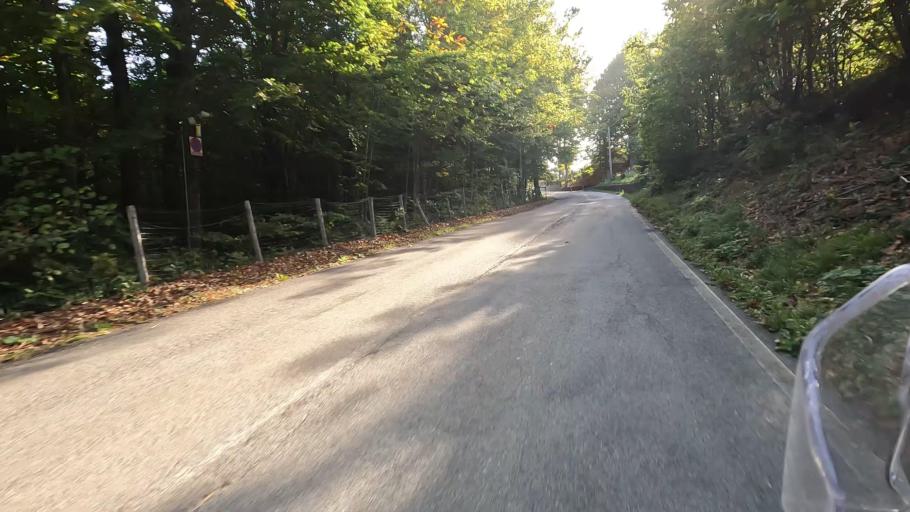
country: IT
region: Liguria
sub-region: Provincia di Savona
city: Urbe
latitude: 44.4706
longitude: 8.5612
